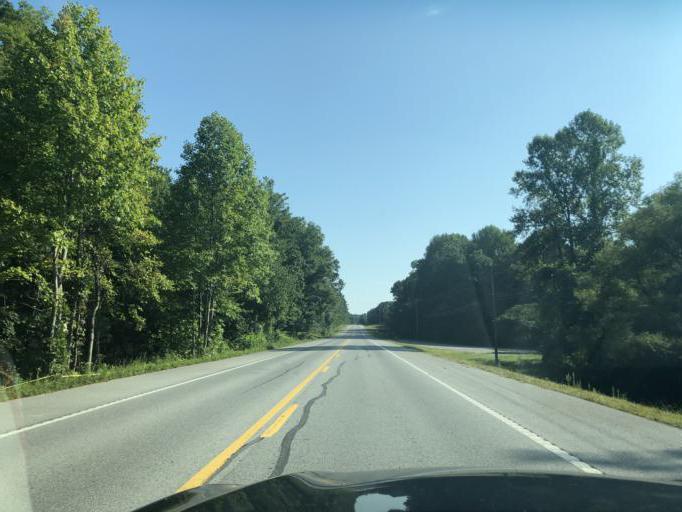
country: US
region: Tennessee
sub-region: Franklin County
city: Sewanee
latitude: 35.1991
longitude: -85.9098
